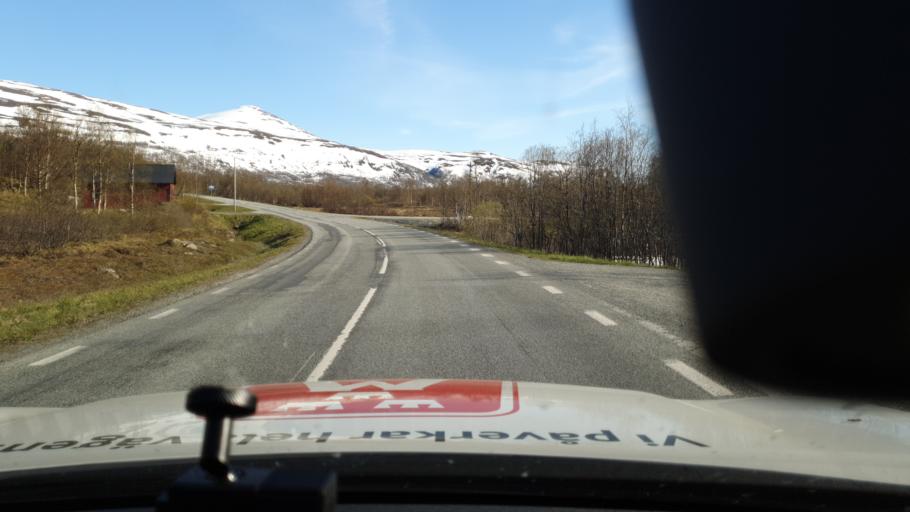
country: NO
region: Nordland
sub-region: Rana
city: Mo i Rana
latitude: 65.9579
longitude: 15.0327
